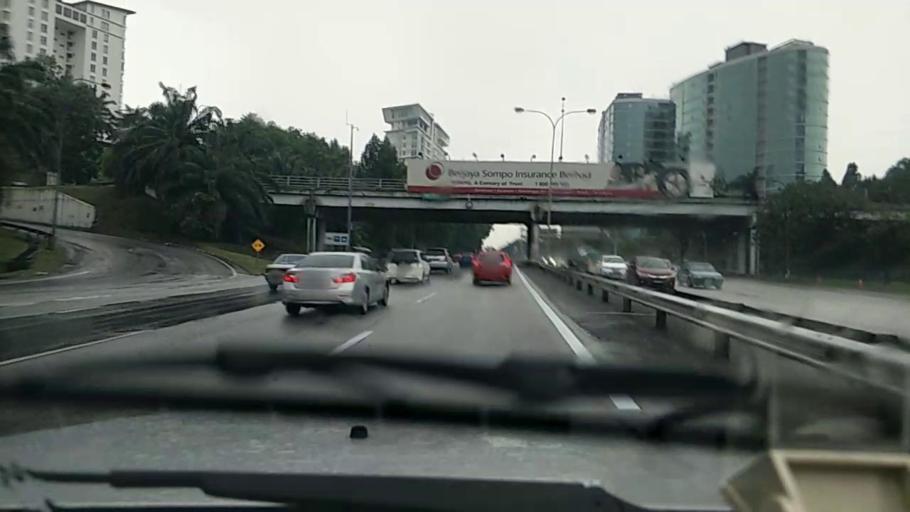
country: MY
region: Kuala Lumpur
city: Kuala Lumpur
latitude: 3.1046
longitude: 101.6942
